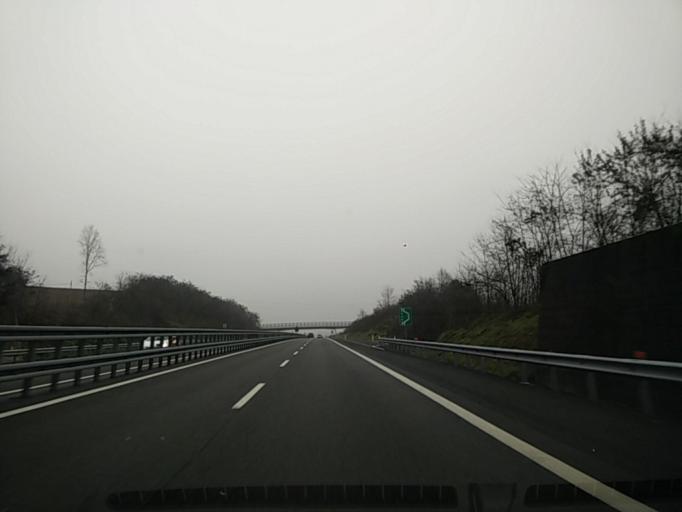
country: IT
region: Piedmont
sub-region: Provincia di Asti
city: Baldichieri d'Asti
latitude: 44.9038
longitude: 8.1085
